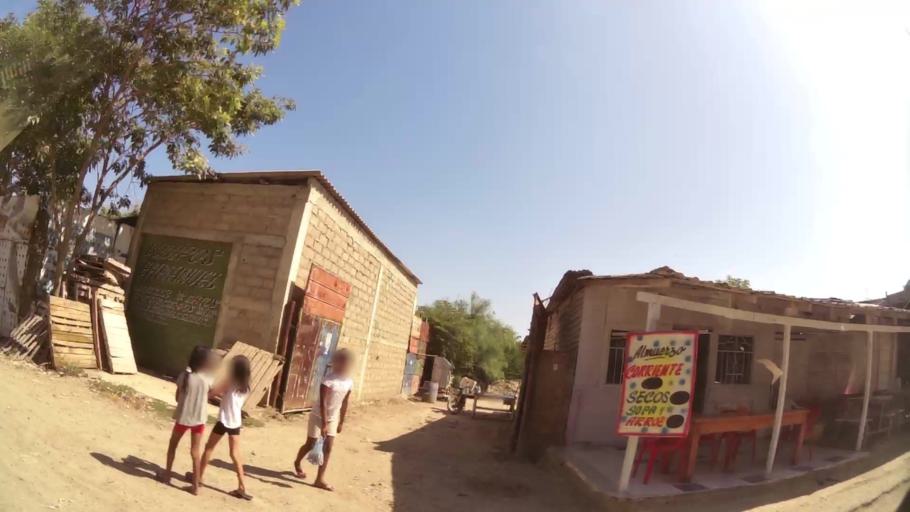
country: CO
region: Bolivar
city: Cartagena
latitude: 10.3664
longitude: -75.4914
